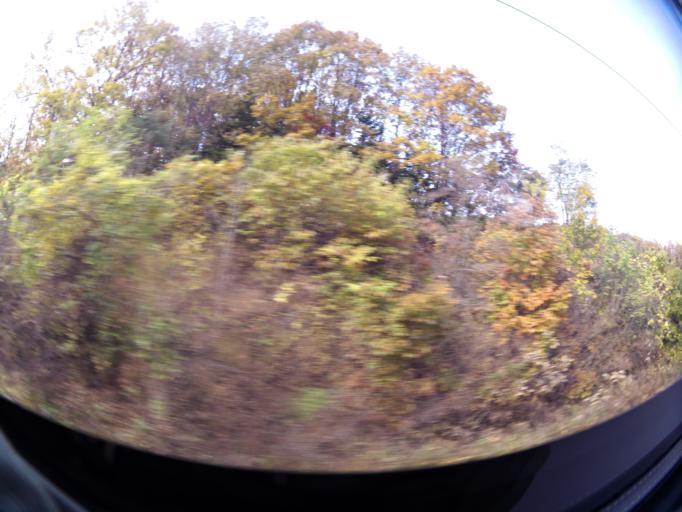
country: KR
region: Gyeongsangbuk-do
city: Gimcheon
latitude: 36.1808
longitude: 128.0079
